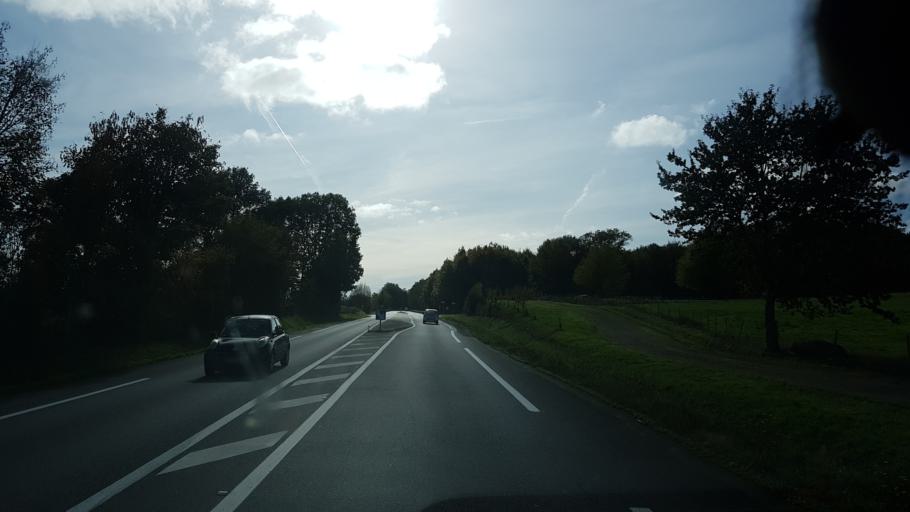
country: FR
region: Poitou-Charentes
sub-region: Departement de la Charente
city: Confolens
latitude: 45.9974
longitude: 0.6319
